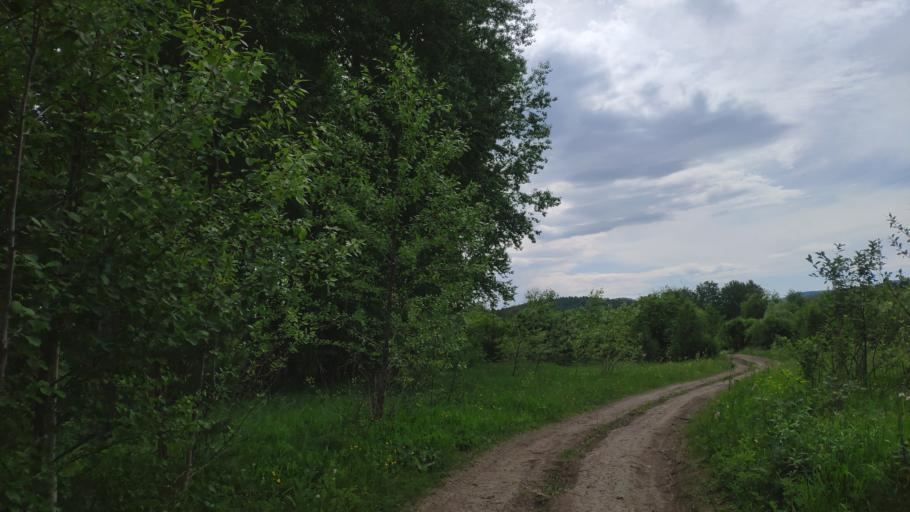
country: RU
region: Bashkortostan
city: Abzakovo
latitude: 53.8155
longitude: 58.6379
